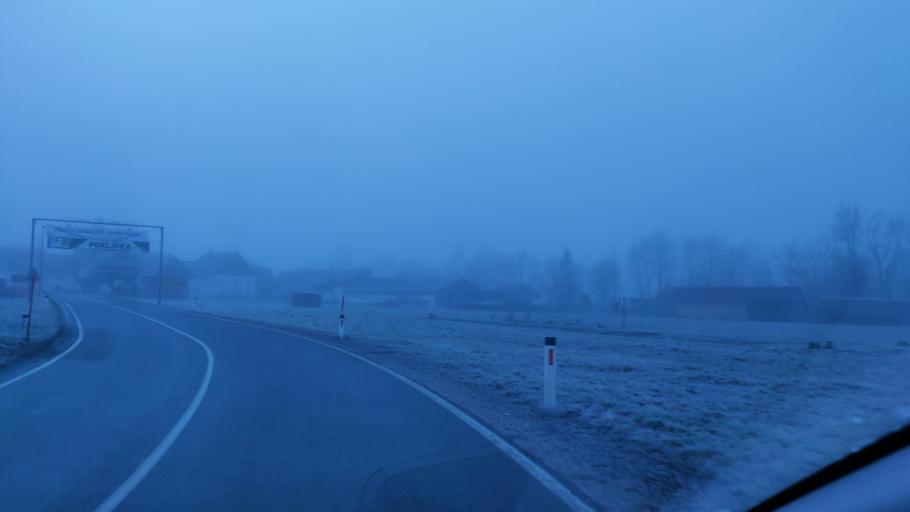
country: SI
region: Bohinj
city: Bohinjska Bistrica
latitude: 46.2770
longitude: 13.9503
